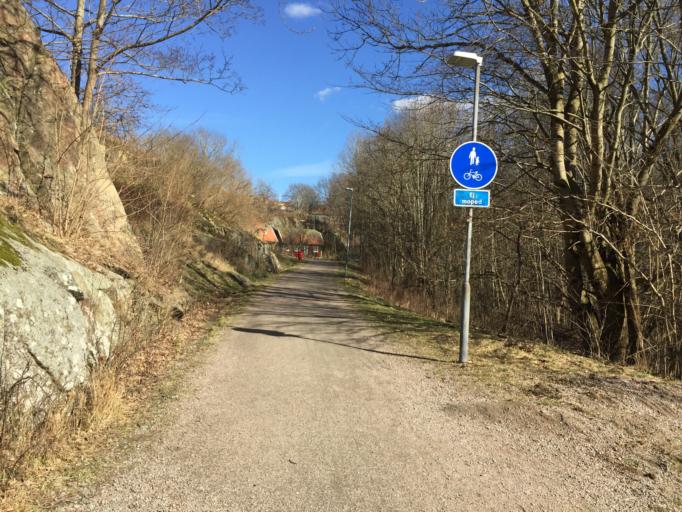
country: SE
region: Vaestra Goetaland
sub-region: Uddevalla Kommun
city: Uddevalla
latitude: 58.3611
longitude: 11.9351
